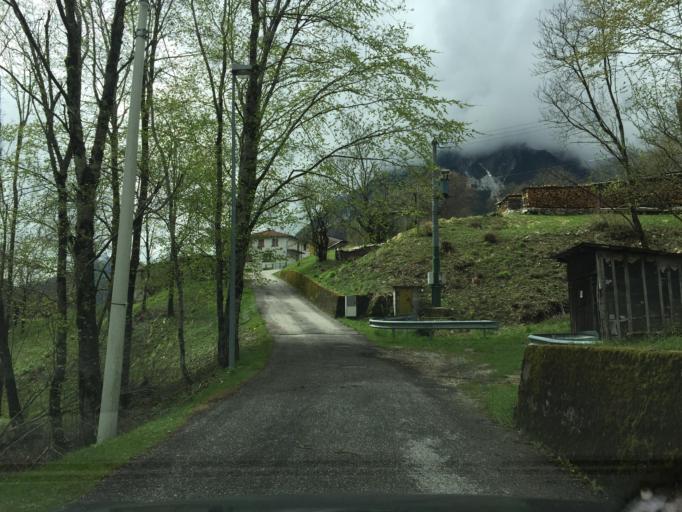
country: IT
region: Friuli Venezia Giulia
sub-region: Provincia di Udine
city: Moggio Udinese
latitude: 46.4859
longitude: 13.1920
